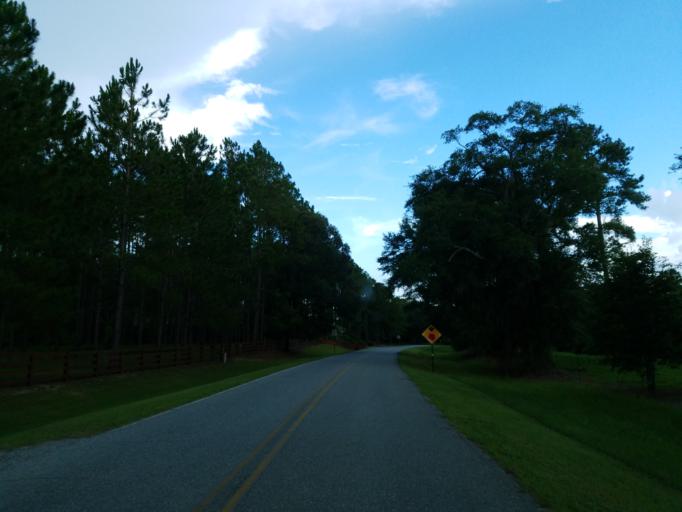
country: US
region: Georgia
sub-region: Tift County
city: Omega
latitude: 31.2571
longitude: -83.5134
